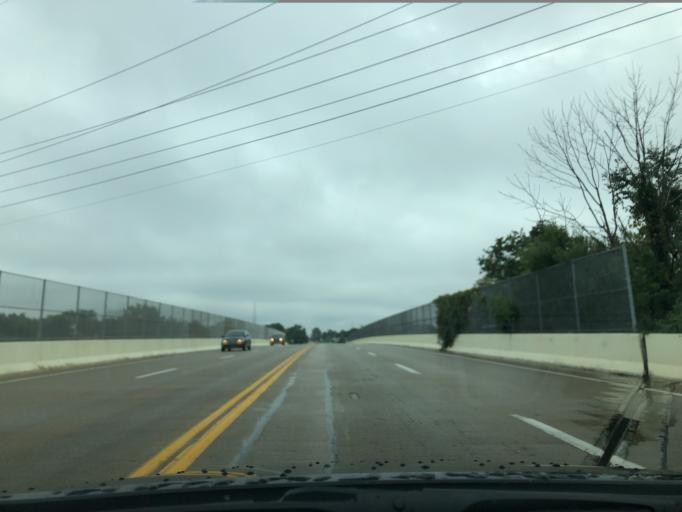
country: US
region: Ohio
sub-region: Hamilton County
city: Highpoint
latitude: 39.2823
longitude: -84.3673
